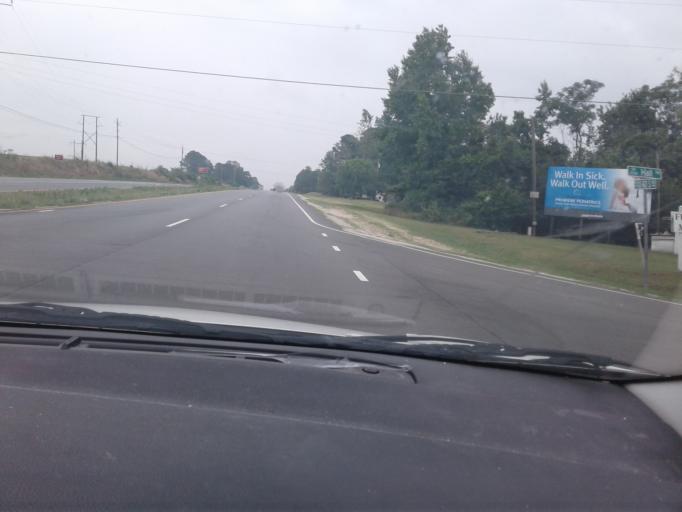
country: US
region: North Carolina
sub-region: Harnett County
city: Buies Creek
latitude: 35.3716
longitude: -78.7084
